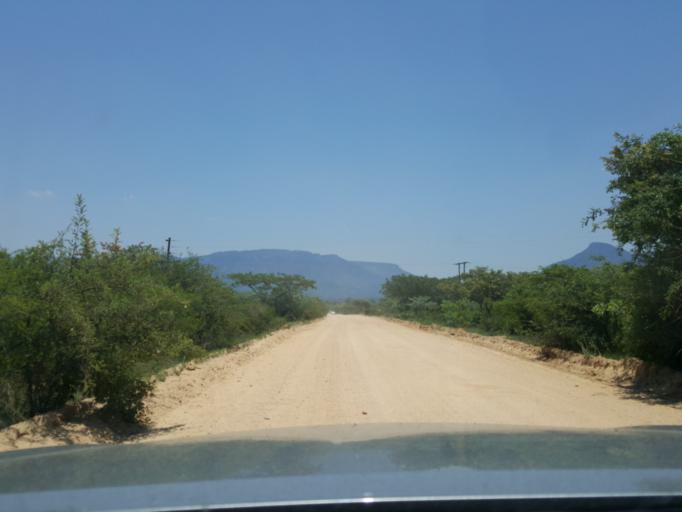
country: ZA
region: Limpopo
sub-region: Mopani District Municipality
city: Hoedspruit
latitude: -24.5686
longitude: 31.0040
